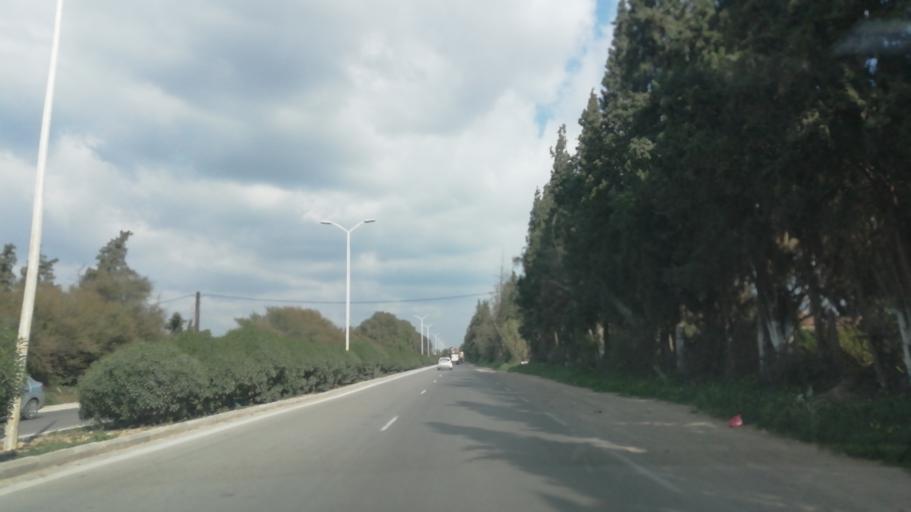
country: DZ
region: Mascara
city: Mascara
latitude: 35.6011
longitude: 0.0842
